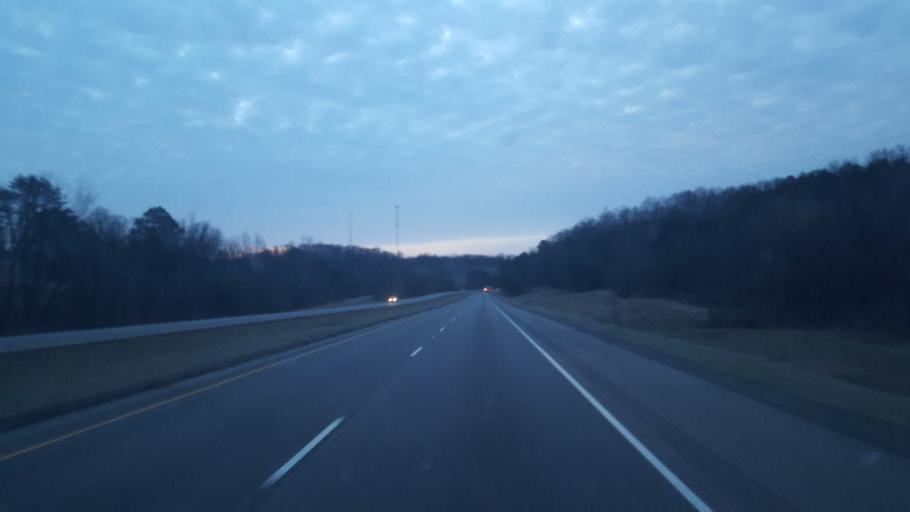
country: US
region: Ohio
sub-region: Jackson County
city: Oak Hill
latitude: 38.9390
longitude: -82.4715
